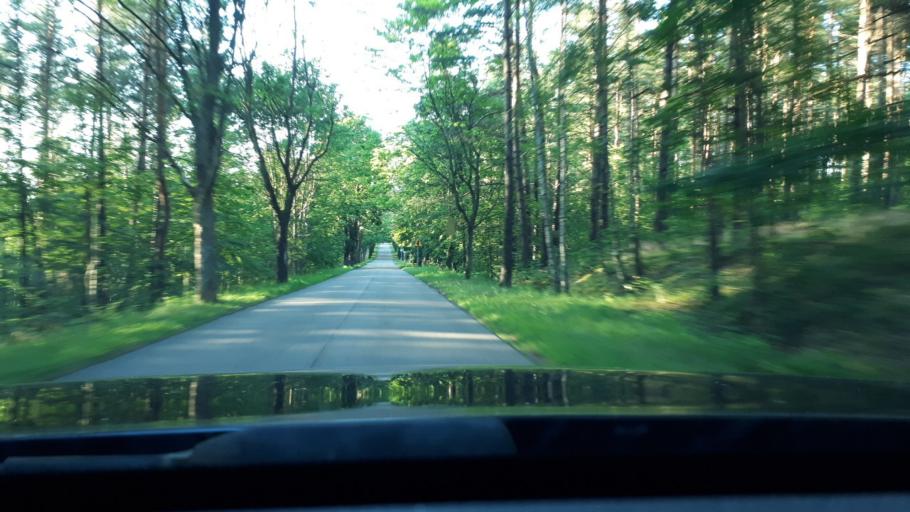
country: PL
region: Warmian-Masurian Voivodeship
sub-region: Powiat olsztynski
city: Stawiguda
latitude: 53.6009
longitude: 20.4228
